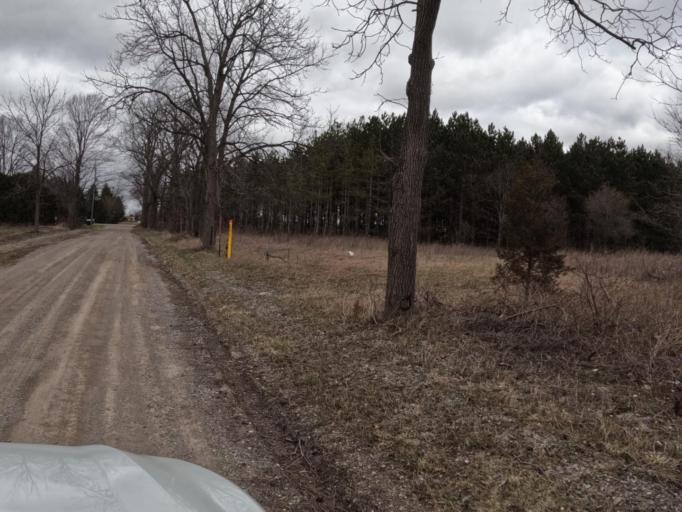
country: CA
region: Ontario
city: Norfolk County
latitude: 42.9688
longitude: -80.3917
